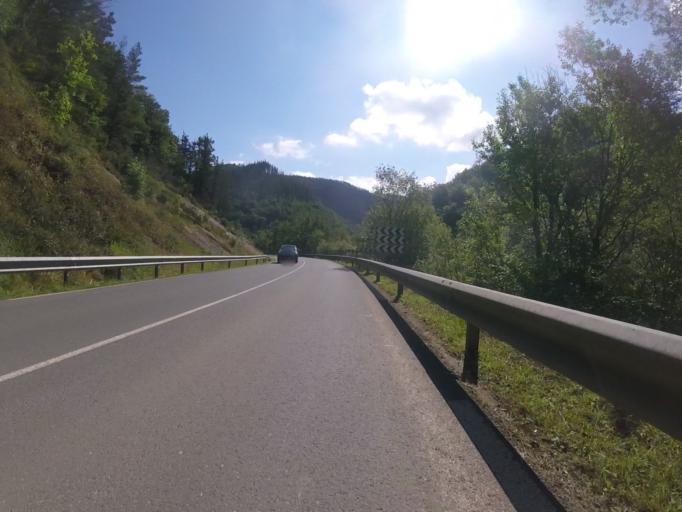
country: ES
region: Basque Country
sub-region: Provincia de Guipuzcoa
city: Beizama
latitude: 43.1137
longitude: -2.2291
